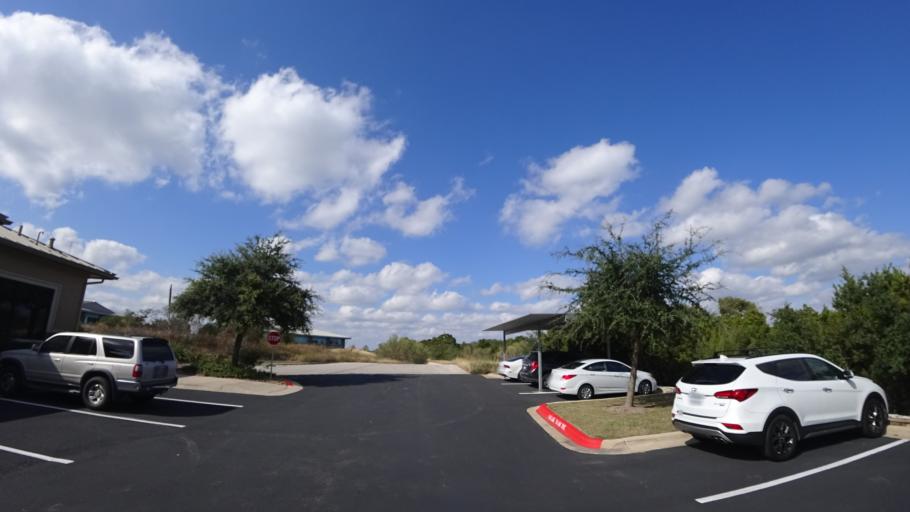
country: US
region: Texas
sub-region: Travis County
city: Barton Creek
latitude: 30.2518
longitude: -97.8925
